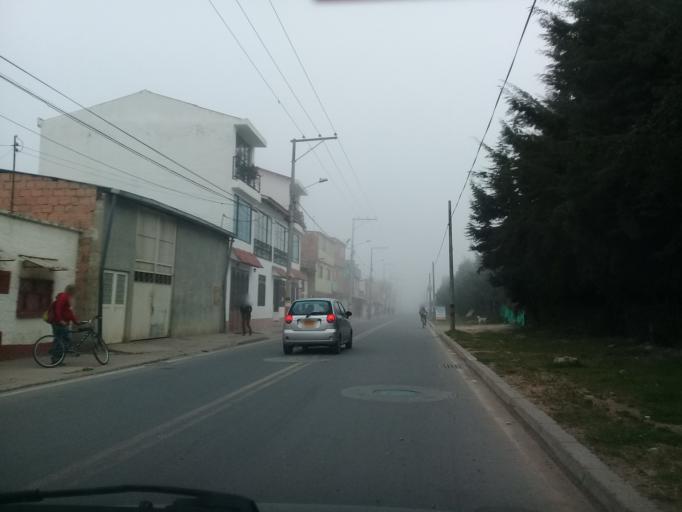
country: CO
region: Cundinamarca
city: Madrid
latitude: 4.7368
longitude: -74.2528
